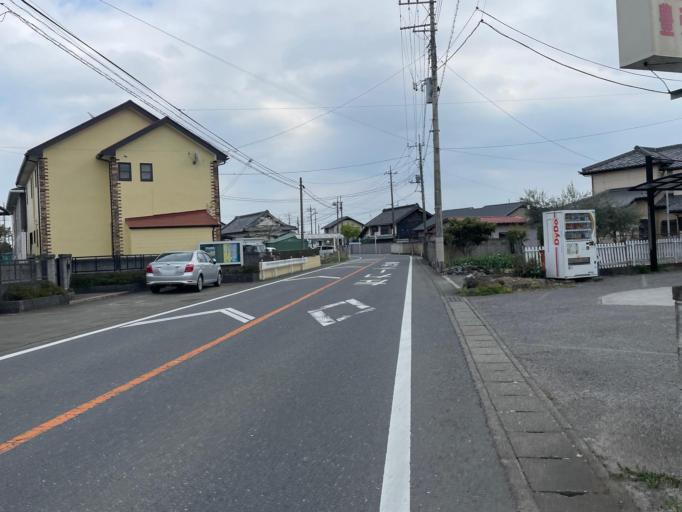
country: JP
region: Gunma
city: Isesaki
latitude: 36.2826
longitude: 139.2007
